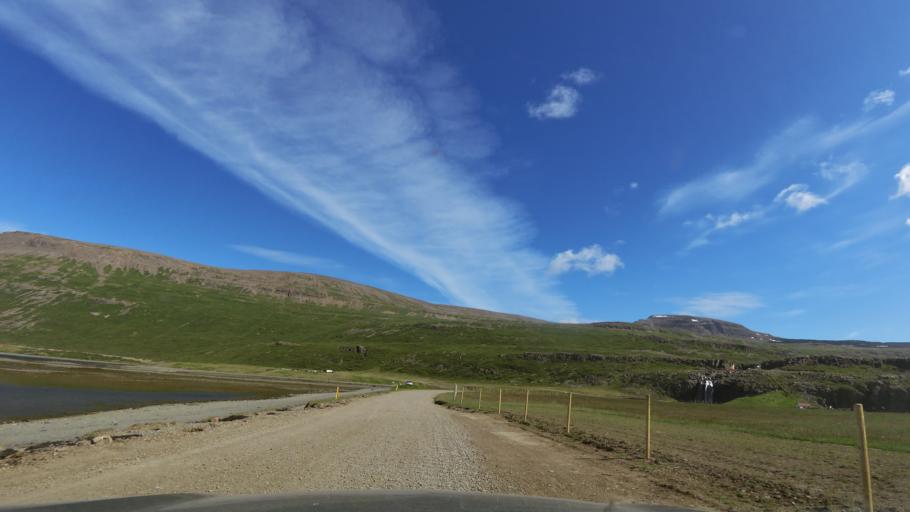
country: IS
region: Westfjords
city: Isafjoerdur
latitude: 65.6038
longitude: -23.5454
